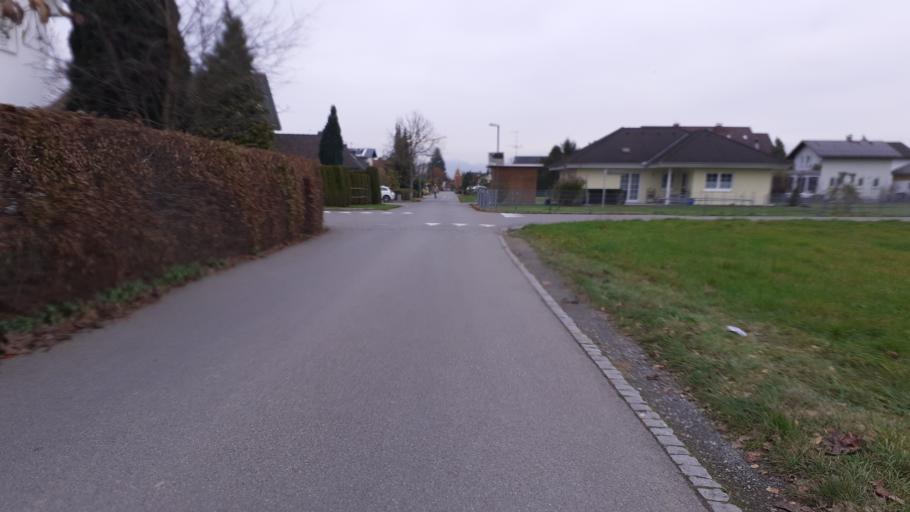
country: AT
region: Vorarlberg
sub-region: Politischer Bezirk Feldkirch
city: Nofels
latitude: 47.2624
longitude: 9.5899
